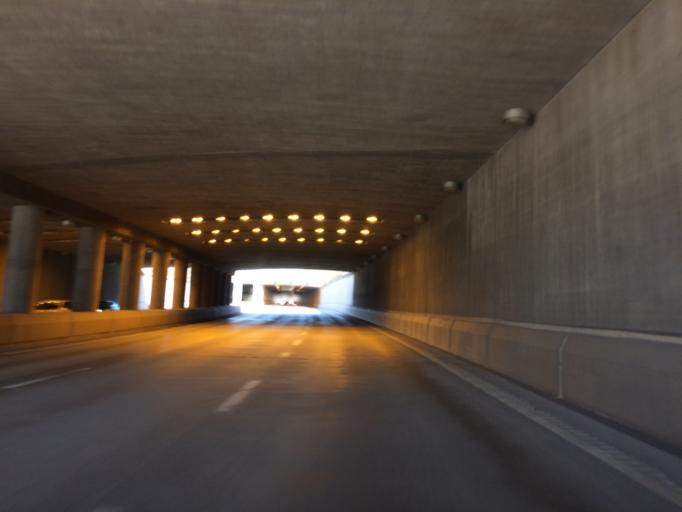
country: SE
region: Stockholm
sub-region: Sollentuna Kommun
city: Sollentuna
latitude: 59.4419
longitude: 17.9342
